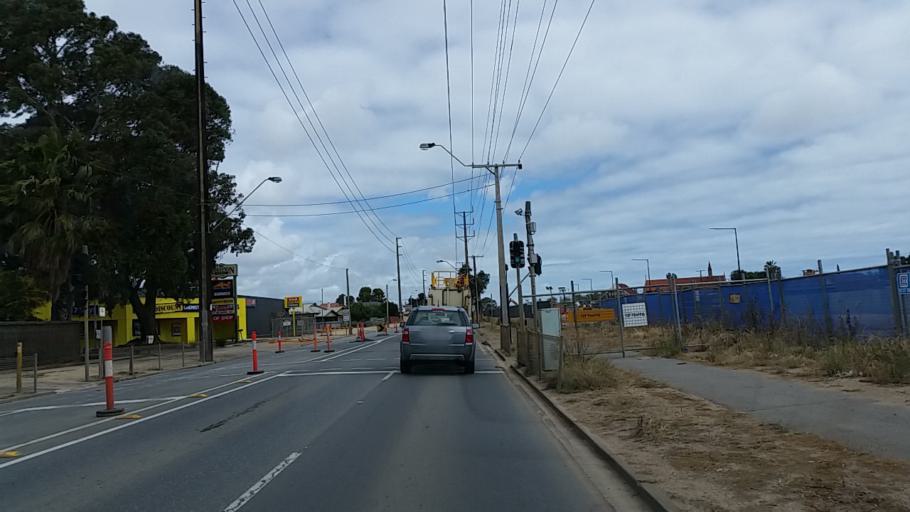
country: AU
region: South Australia
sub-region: Charles Sturt
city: Allenby Gardens
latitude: -34.8932
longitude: 138.5687
